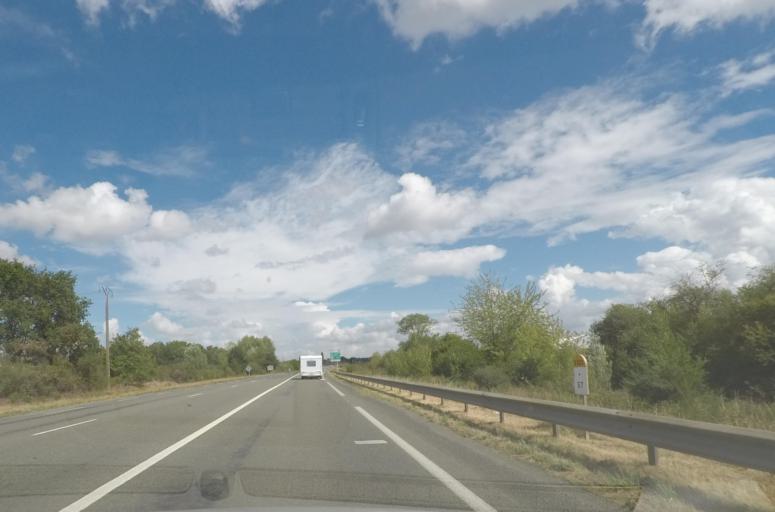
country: FR
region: Pays de la Loire
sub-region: Departement de la Sarthe
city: Spay
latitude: 47.9352
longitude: 0.1613
